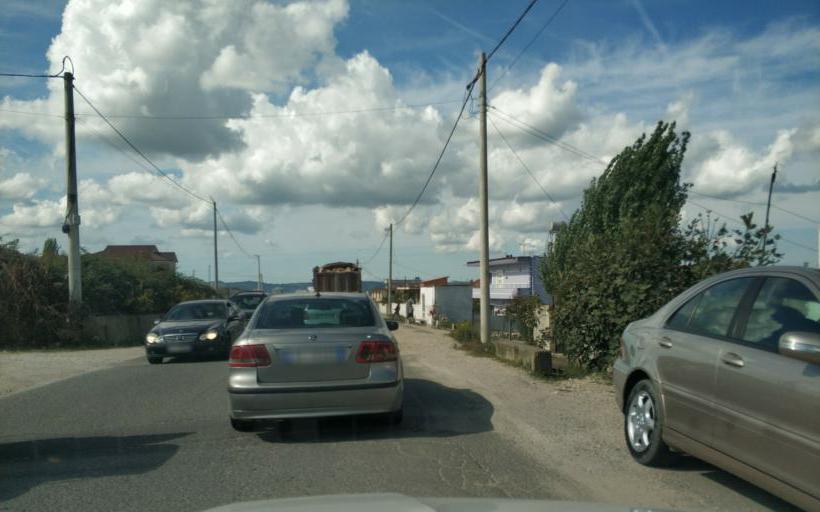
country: AL
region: Durres
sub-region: Rrethi i Krujes
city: Fushe-Kruje
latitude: 41.4778
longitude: 19.7404
